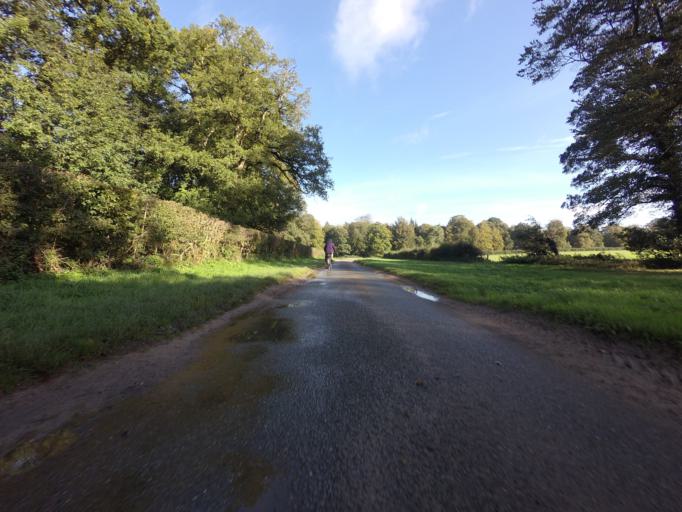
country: GB
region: England
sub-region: Norfolk
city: Dersingham
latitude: 52.8187
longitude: 0.6398
